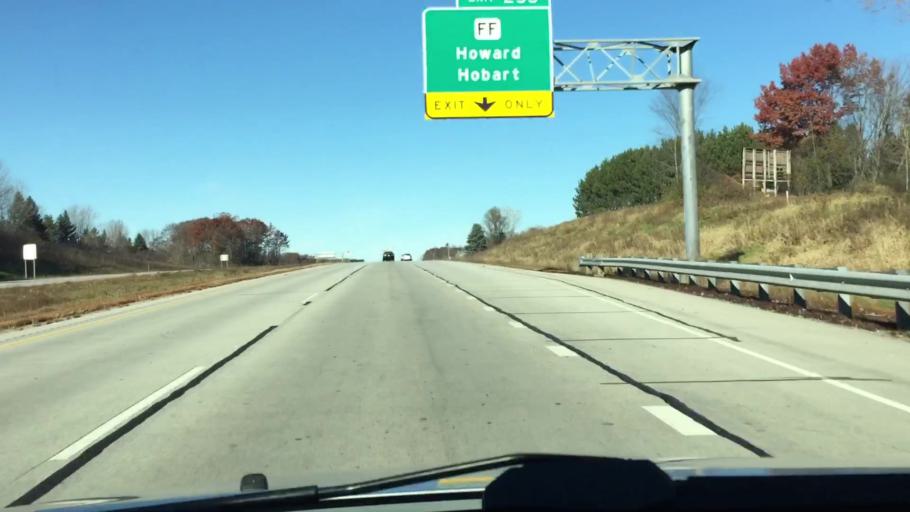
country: US
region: Wisconsin
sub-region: Brown County
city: Howard
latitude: 44.5557
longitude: -88.1183
